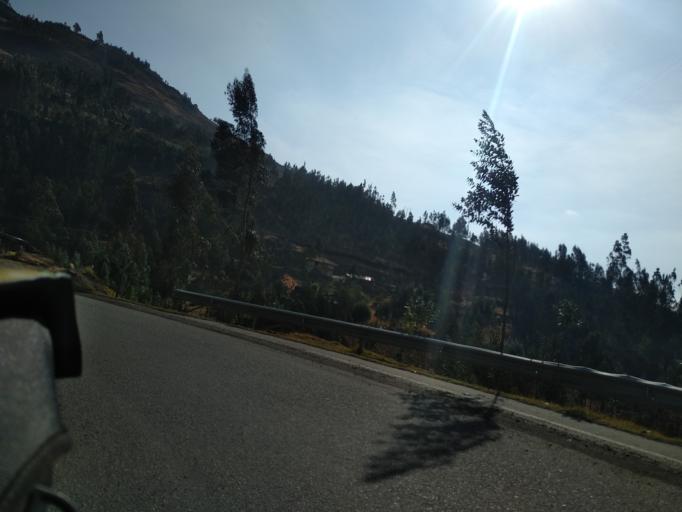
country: PE
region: La Libertad
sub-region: Provincia de Otuzco
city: Mache
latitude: -7.9971
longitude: -78.5066
